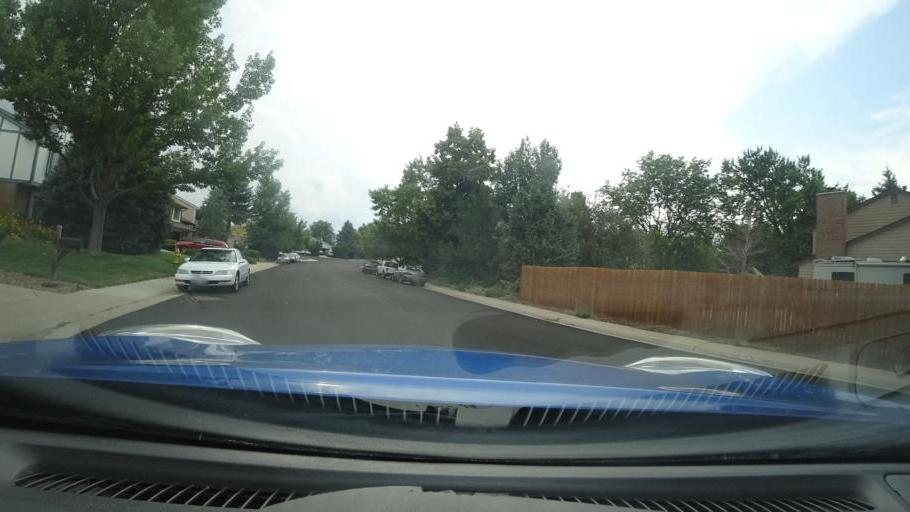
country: US
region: Colorado
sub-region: Adams County
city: Aurora
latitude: 39.6900
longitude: -104.8118
